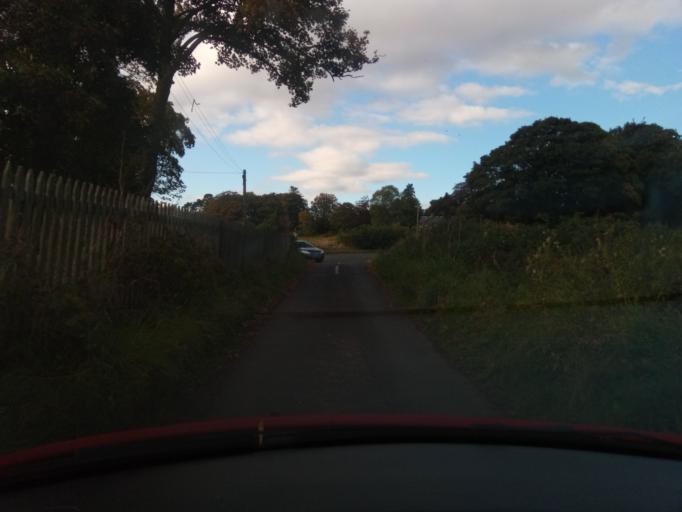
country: GB
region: Scotland
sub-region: The Scottish Borders
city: Kelso
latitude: 55.5279
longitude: -2.3570
